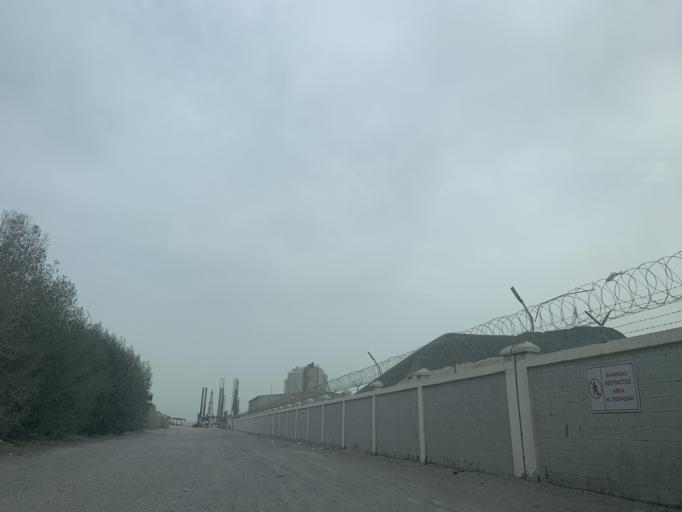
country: BH
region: Muharraq
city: Al Hadd
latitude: 26.2066
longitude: 50.6697
